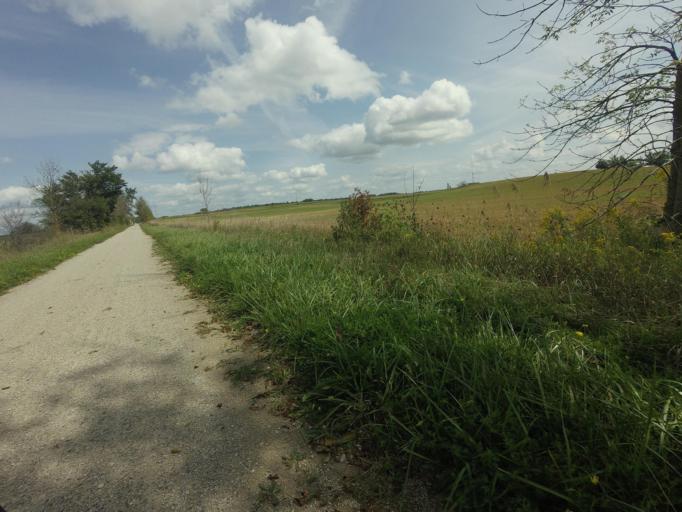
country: CA
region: Ontario
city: Waterloo
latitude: 43.5892
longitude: -80.6980
